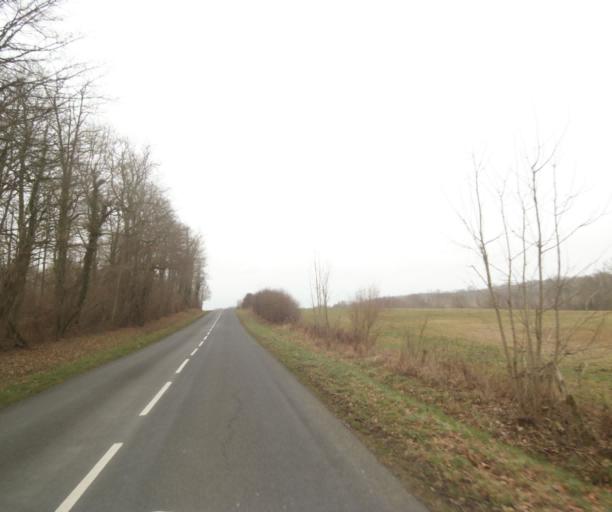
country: FR
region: Champagne-Ardenne
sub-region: Departement de la Marne
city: Pargny-sur-Saulx
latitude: 48.7395
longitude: 4.8709
